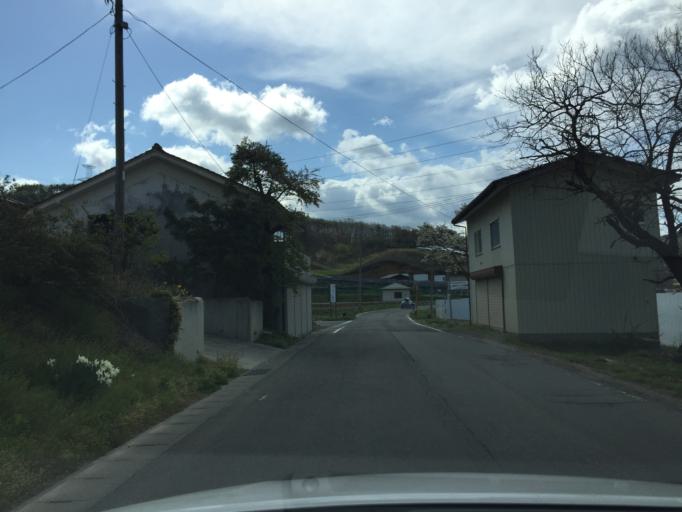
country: JP
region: Fukushima
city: Funehikimachi-funehiki
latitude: 37.6138
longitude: 140.6563
